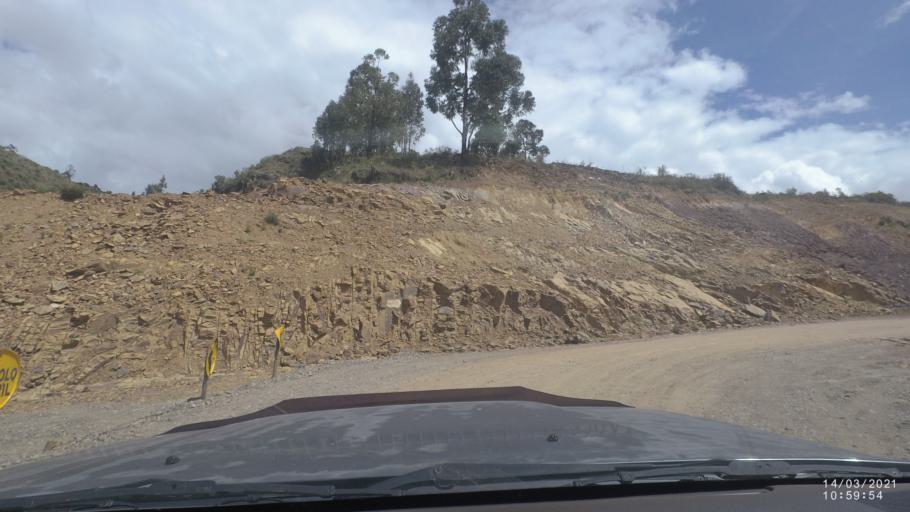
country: BO
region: Cochabamba
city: Tarata
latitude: -17.8073
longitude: -65.9633
